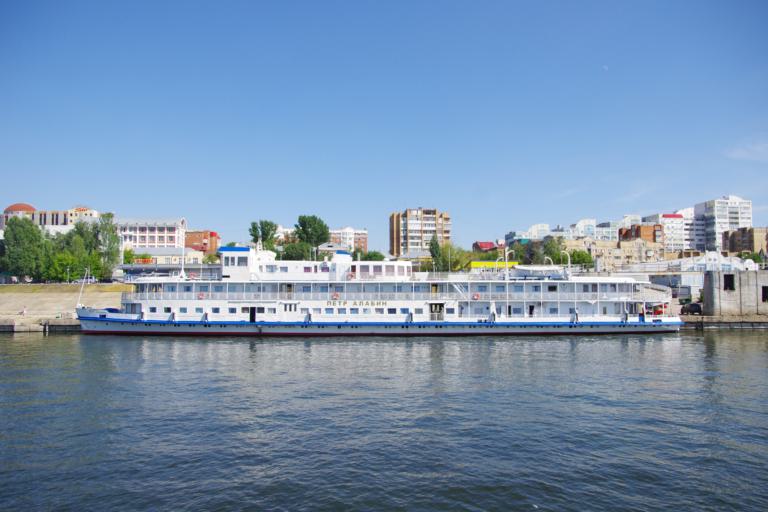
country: RU
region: Samara
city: Rozhdestveno
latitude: 53.1847
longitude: 50.0736
